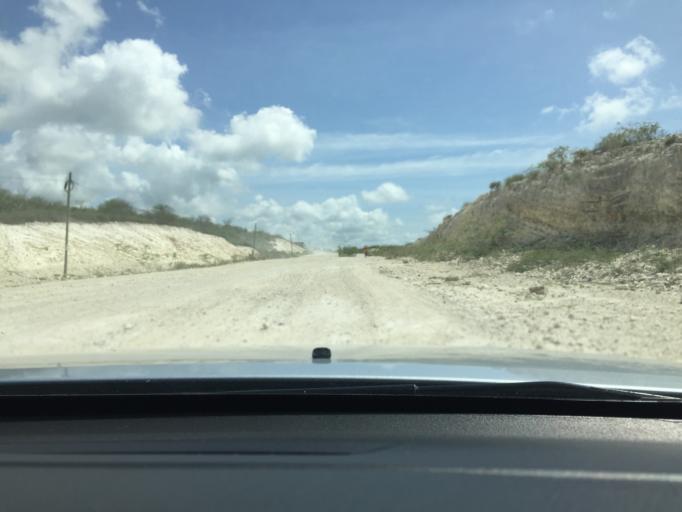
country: HT
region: Sud
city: Aquin
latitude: 18.2368
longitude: -73.2694
